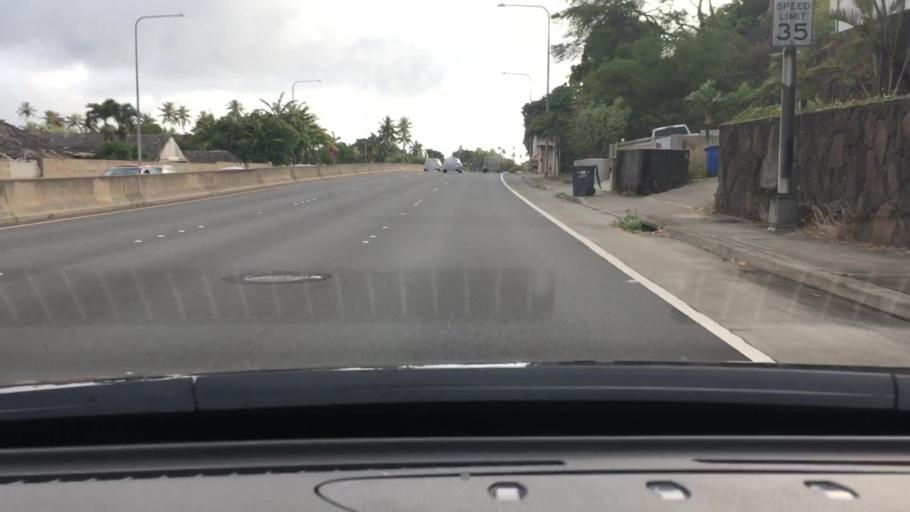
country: US
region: Hawaii
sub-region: Honolulu County
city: Waimanalo Beach
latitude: 21.2849
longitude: -157.7269
